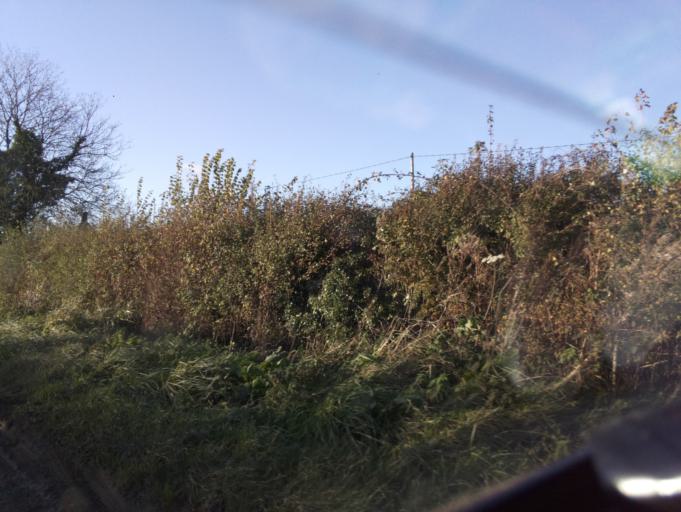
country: GB
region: England
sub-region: Somerset
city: Milborne Port
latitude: 50.9964
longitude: -2.4516
